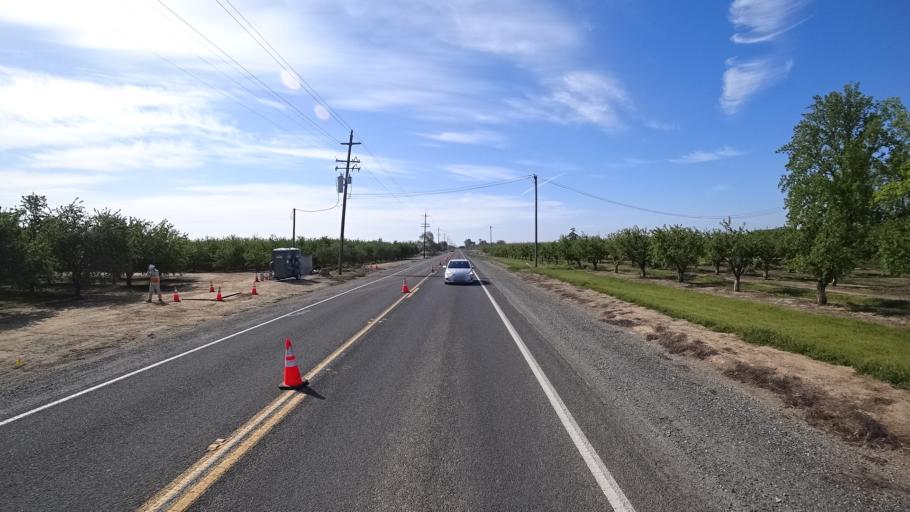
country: US
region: California
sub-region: Glenn County
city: Hamilton City
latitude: 39.6514
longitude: -122.0080
